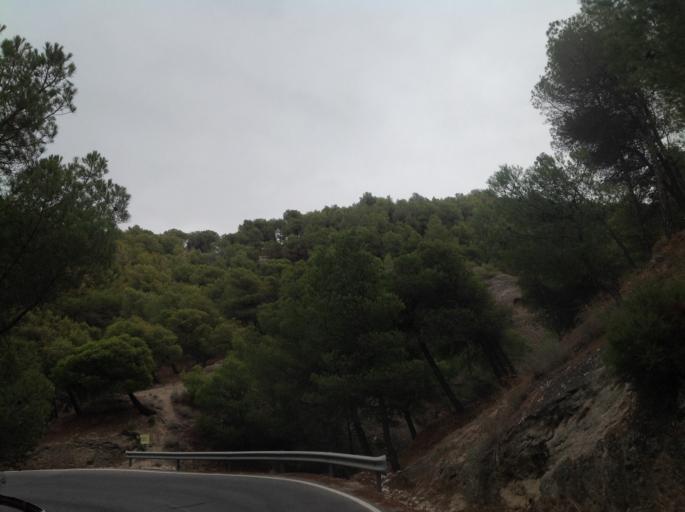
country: ES
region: Andalusia
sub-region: Provincia de Malaga
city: Ardales
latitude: 36.9169
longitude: -4.8039
